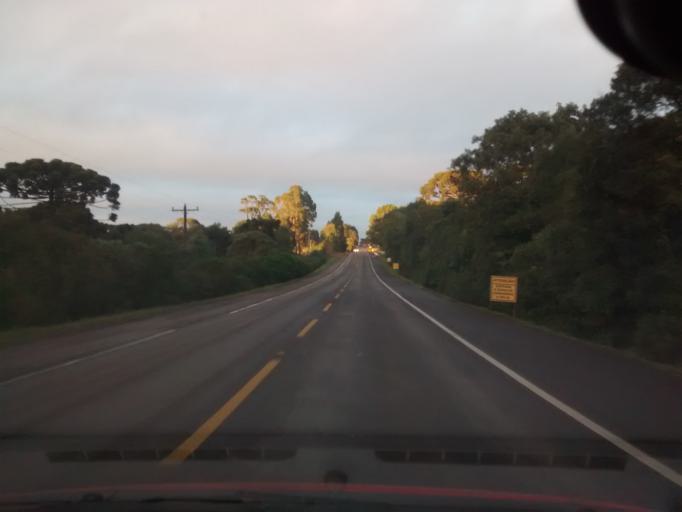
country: BR
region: Rio Grande do Sul
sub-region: Vacaria
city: Estrela
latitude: -28.2739
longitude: -50.7956
